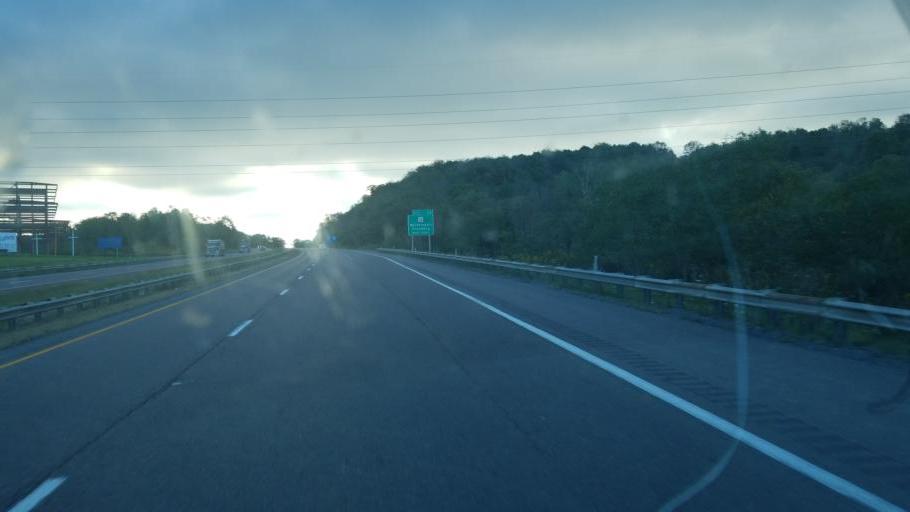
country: US
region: Maryland
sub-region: Allegany County
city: Frostburg
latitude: 39.6335
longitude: -78.9319
